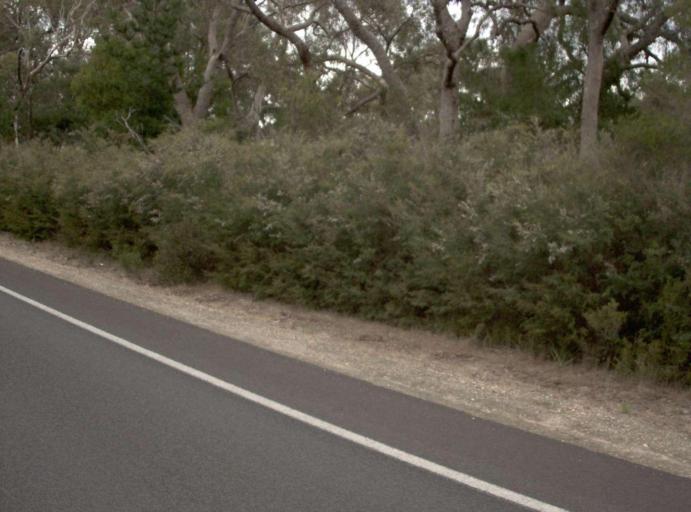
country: AU
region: Victoria
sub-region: Wellington
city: Sale
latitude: -38.1874
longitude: 147.0806
